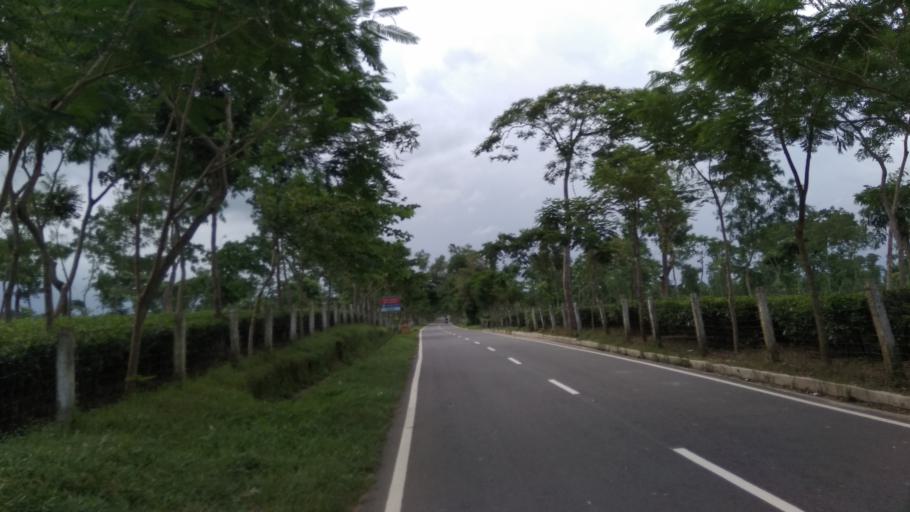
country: IN
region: Tripura
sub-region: Dhalai
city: Kamalpur
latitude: 24.3019
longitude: 91.7471
